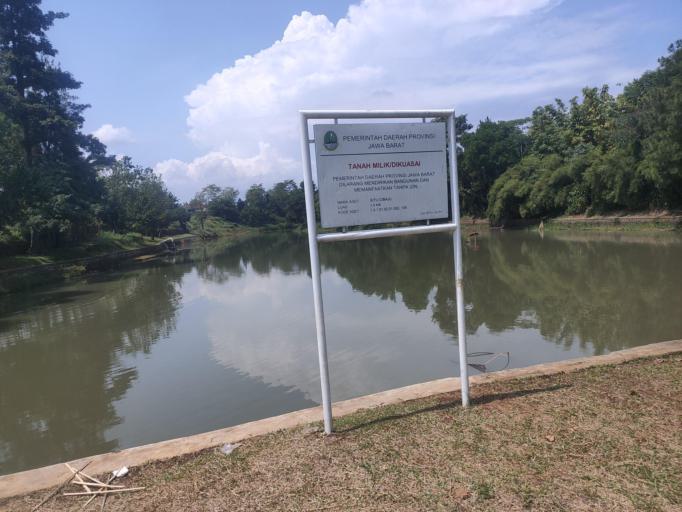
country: ID
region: West Java
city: Ciampea
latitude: -6.5245
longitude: 106.6999
